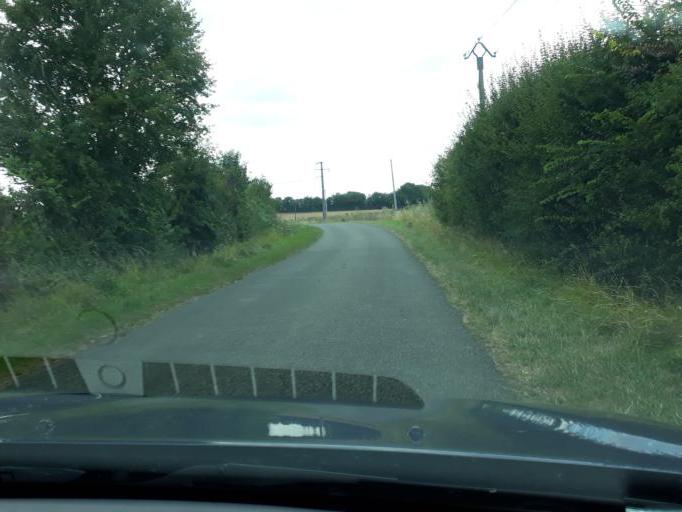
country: FR
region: Centre
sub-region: Departement du Cher
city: Jouet-sur-l'Aubois
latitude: 46.9846
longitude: 2.9231
